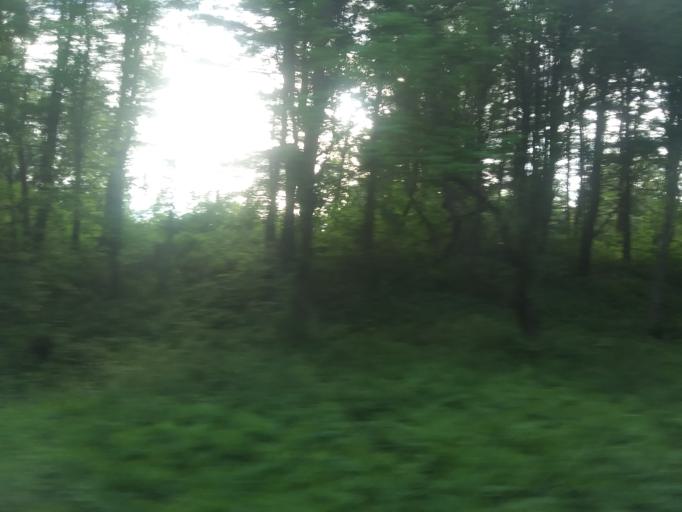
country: US
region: Massachusetts
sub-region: Franklin County
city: Shelburne Falls
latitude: 42.6117
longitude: -72.7621
